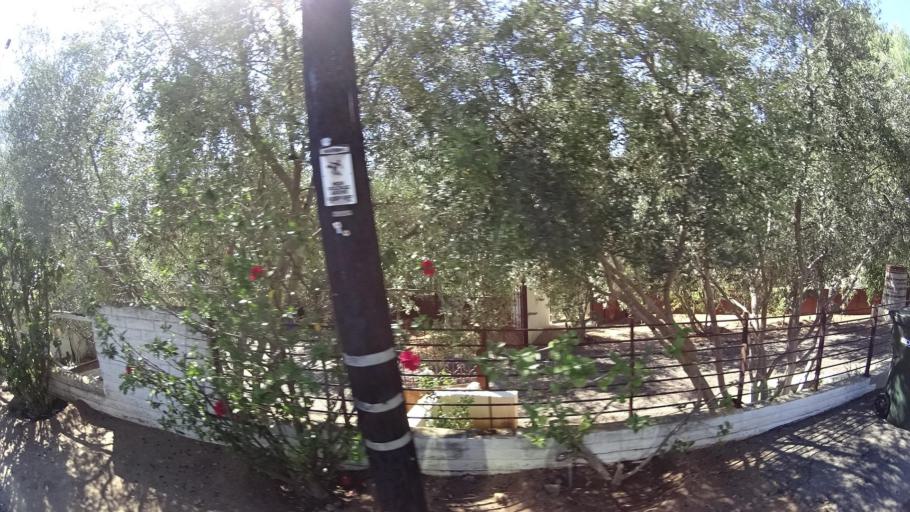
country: US
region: California
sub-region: San Diego County
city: Casa de Oro-Mount Helix
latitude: 32.7601
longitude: -116.9633
